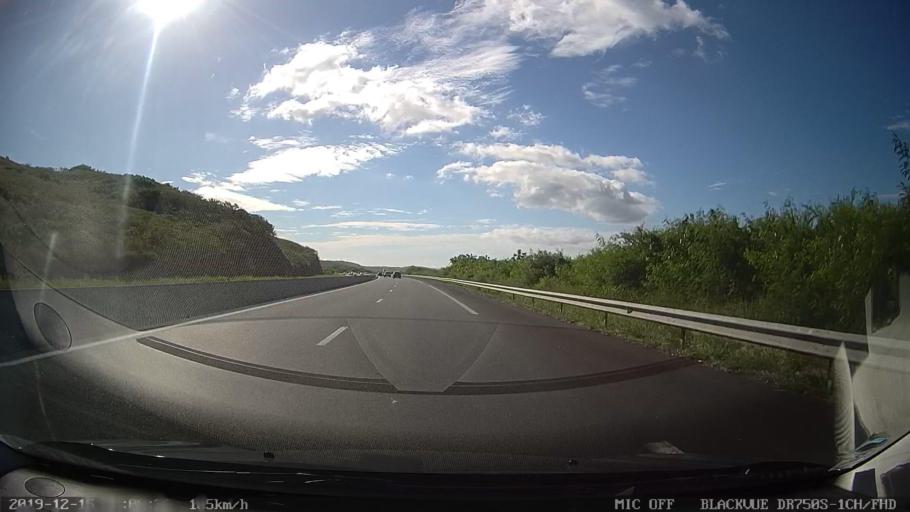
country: RE
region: Reunion
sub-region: Reunion
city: Les Avirons
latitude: -21.2416
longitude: 55.3183
